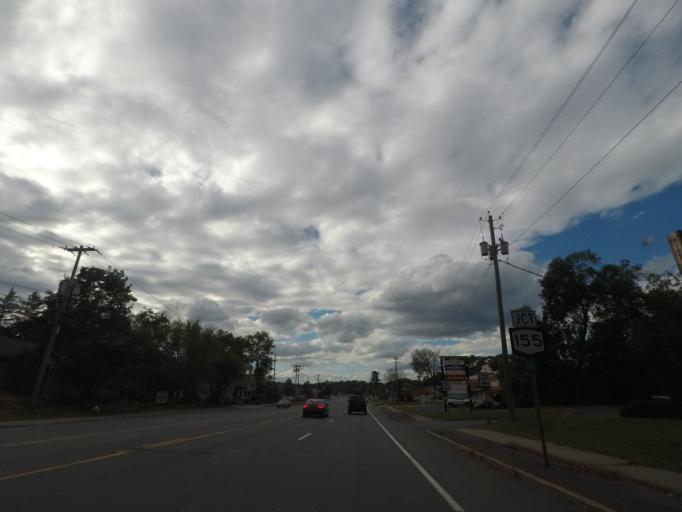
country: US
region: New York
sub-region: Albany County
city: Westmere
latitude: 42.6968
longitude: -73.8850
